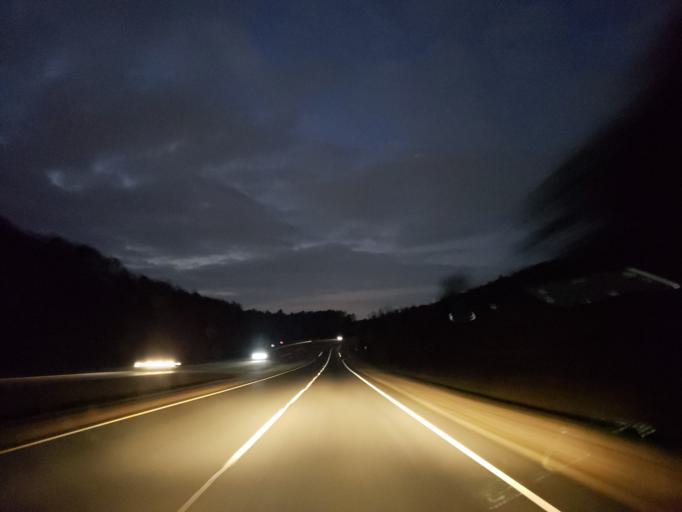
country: US
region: Georgia
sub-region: Polk County
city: Rockmart
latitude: 33.9885
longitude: -85.0213
